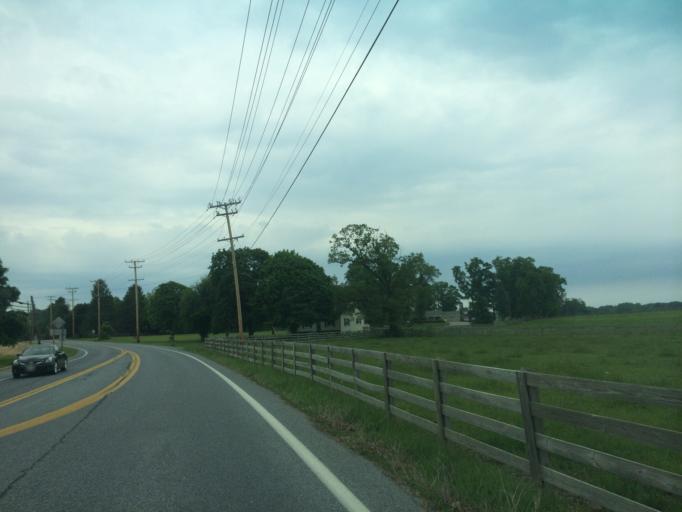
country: US
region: Maryland
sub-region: Howard County
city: Fulton
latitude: 39.1526
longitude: -76.9237
